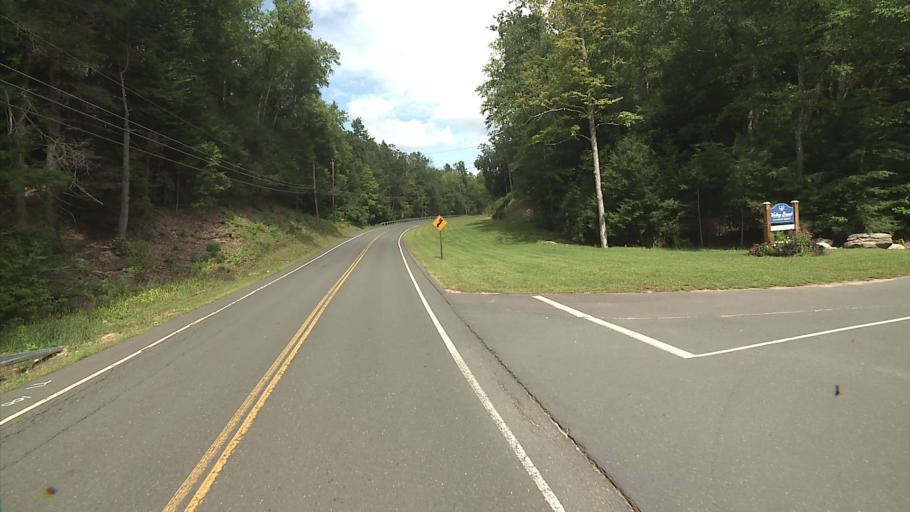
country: US
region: Connecticut
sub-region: Hartford County
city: North Granby
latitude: 42.0119
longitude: -72.8478
